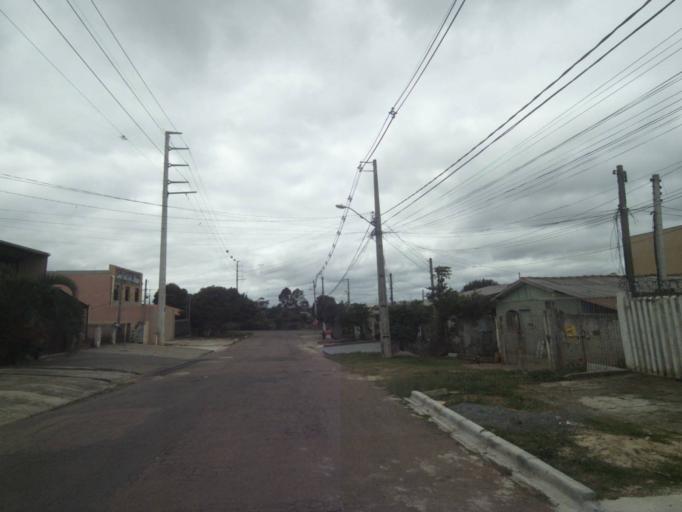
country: BR
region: Parana
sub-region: Sao Jose Dos Pinhais
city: Sao Jose dos Pinhais
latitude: -25.5515
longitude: -49.2592
